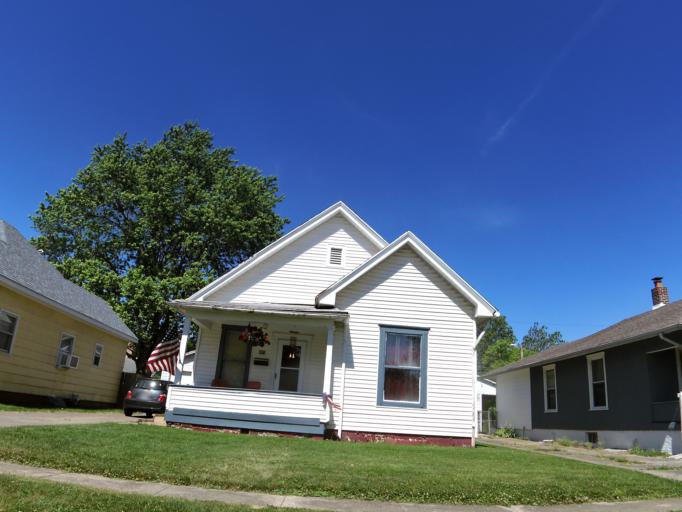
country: US
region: Illinois
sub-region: Vermilion County
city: Danville
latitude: 40.1340
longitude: -87.5982
